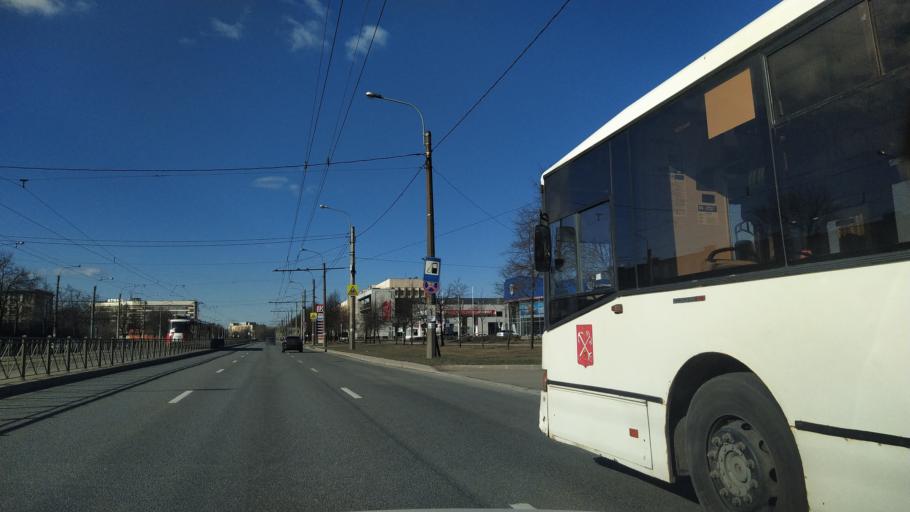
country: RU
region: St.-Petersburg
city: Kupchino
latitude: 59.8883
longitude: 30.3630
